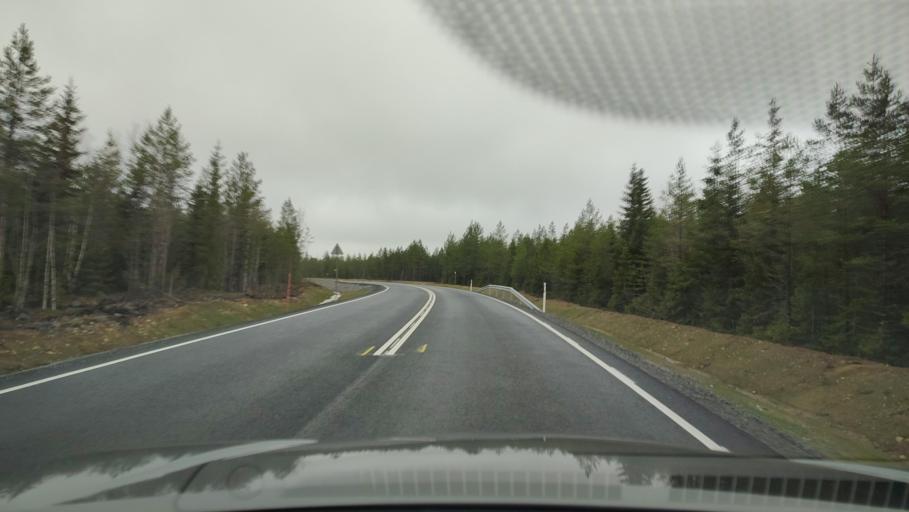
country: FI
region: Southern Ostrobothnia
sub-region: Suupohja
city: Kauhajoki
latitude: 62.2929
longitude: 22.0532
